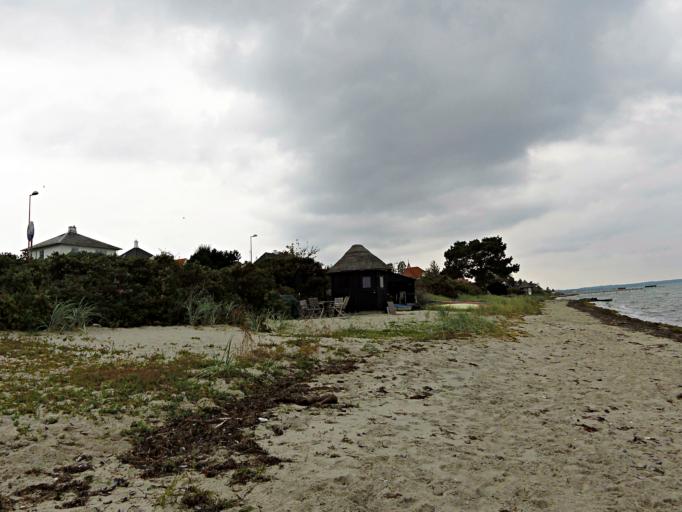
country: DK
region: Capital Region
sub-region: Horsholm Kommune
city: Horsholm
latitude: 55.8891
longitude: 12.5411
